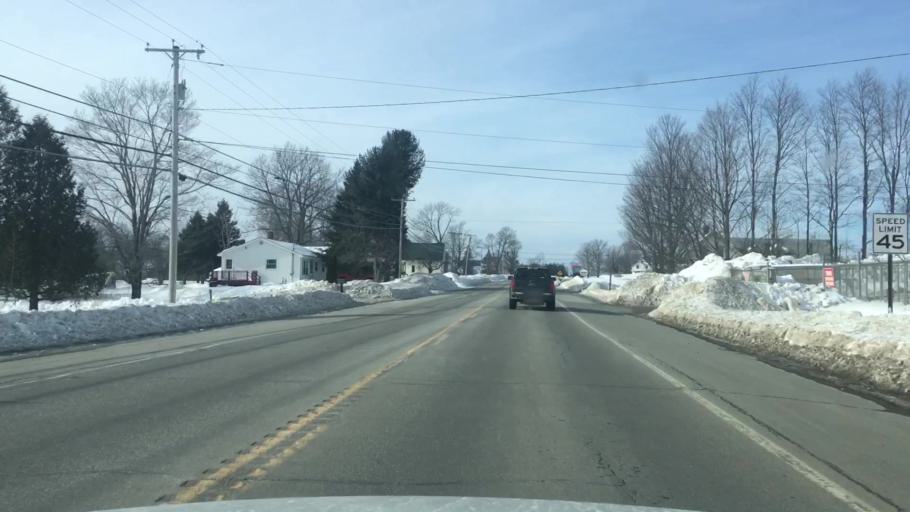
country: US
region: Maine
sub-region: Penobscot County
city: Charleston
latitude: 44.9899
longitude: -69.0150
